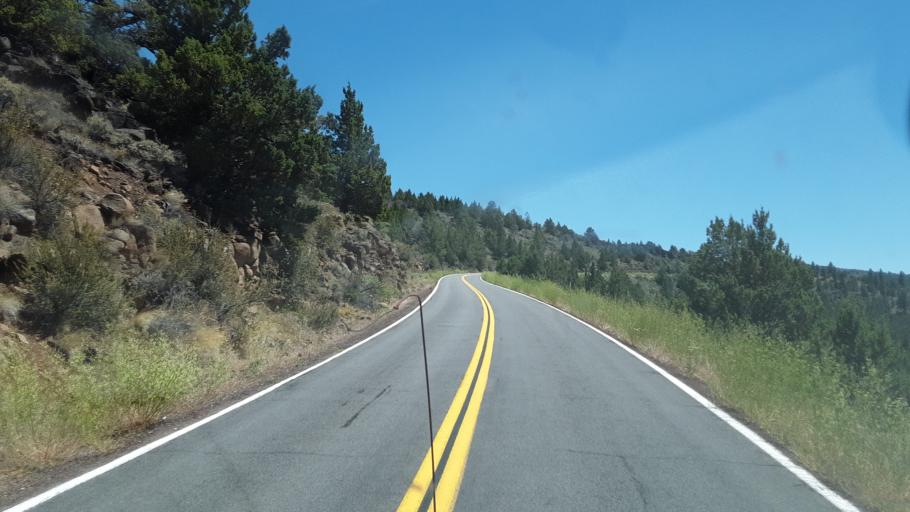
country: US
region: California
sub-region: Lassen County
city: Susanville
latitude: 40.6480
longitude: -120.6575
